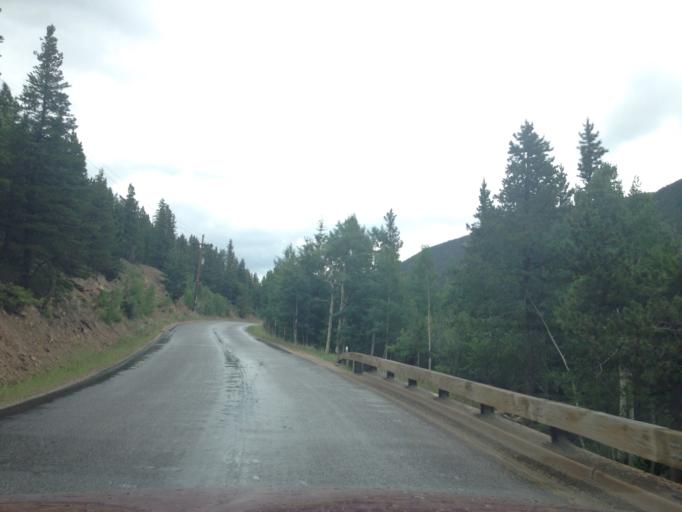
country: US
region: Colorado
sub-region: Clear Creek County
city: Georgetown
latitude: 39.6944
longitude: -105.6967
